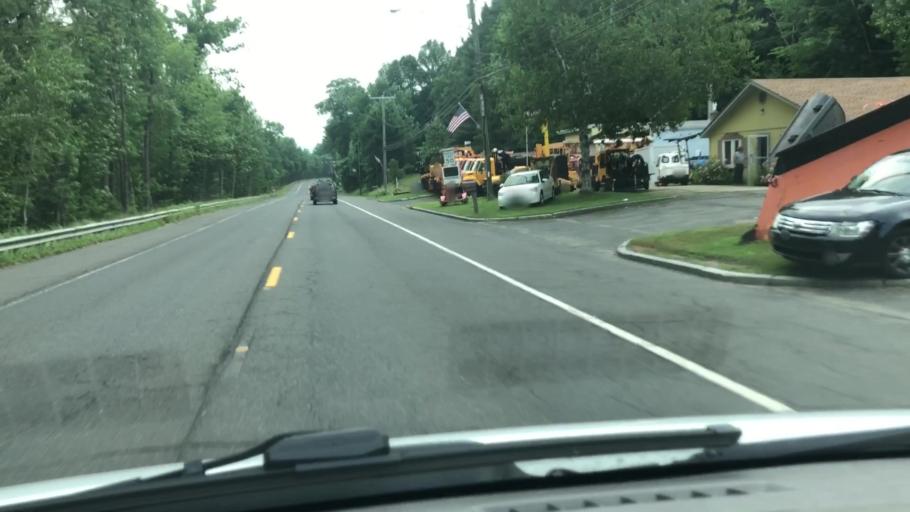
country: US
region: Massachusetts
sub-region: Berkshire County
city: Lanesborough
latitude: 42.5027
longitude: -73.1956
